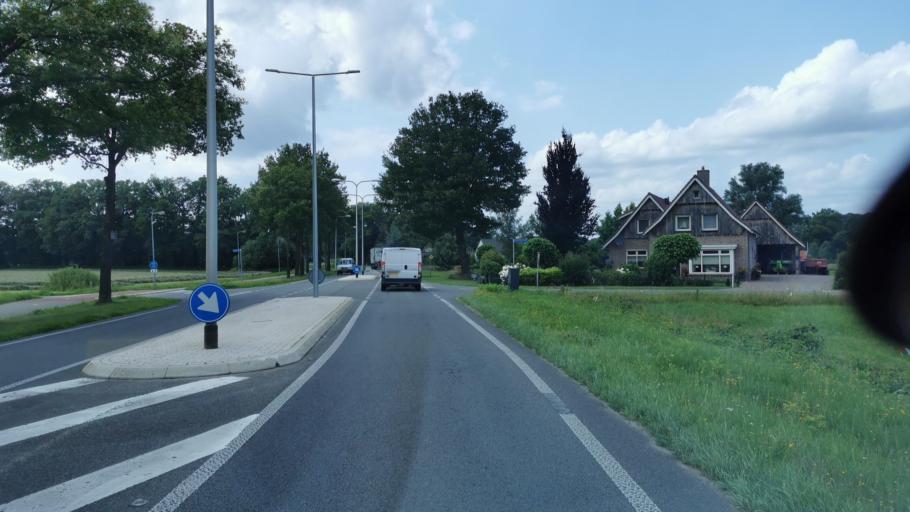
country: NL
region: Overijssel
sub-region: Gemeente Losser
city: Losser
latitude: 52.2712
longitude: 6.9852
